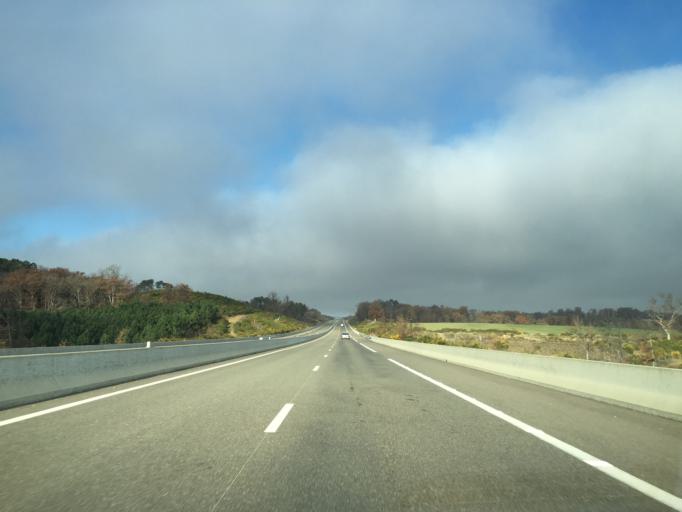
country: FR
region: Aquitaine
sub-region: Departement des Landes
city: Villeneuve-de-Marsan
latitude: 43.8067
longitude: -0.3047
